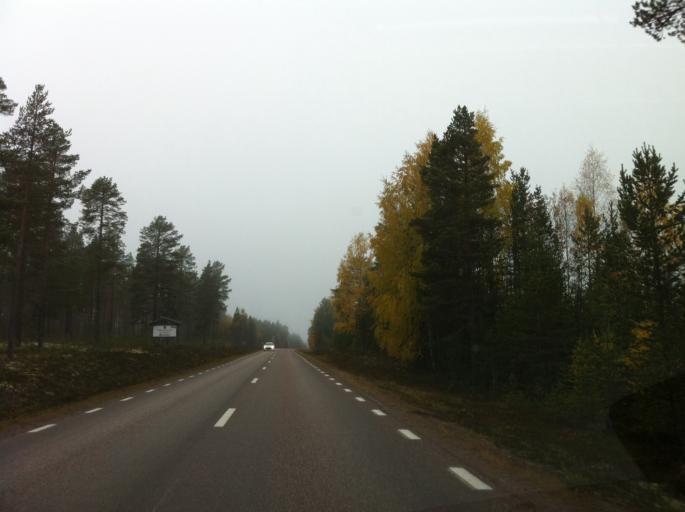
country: NO
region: Hedmark
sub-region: Trysil
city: Innbygda
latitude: 61.6951
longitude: 13.1129
